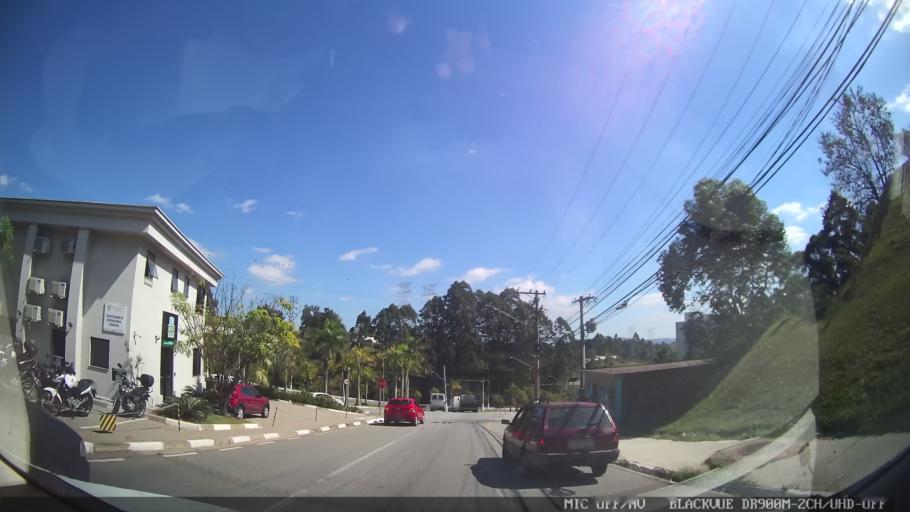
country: BR
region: Sao Paulo
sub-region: Carapicuiba
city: Carapicuiba
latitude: -23.4778
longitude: -46.8320
